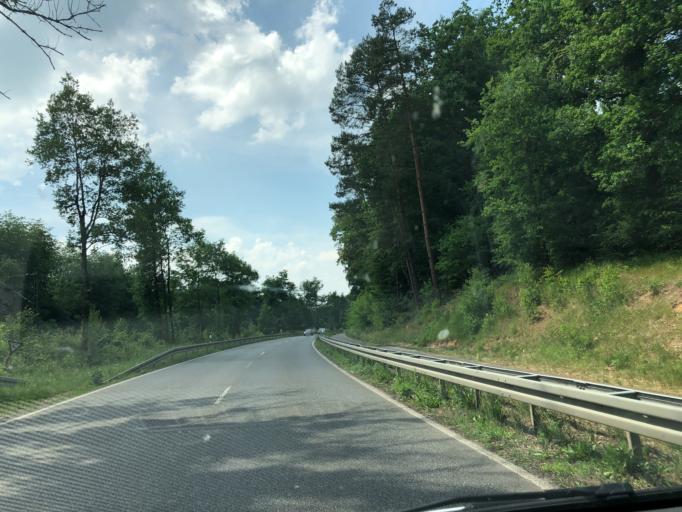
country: DE
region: Hesse
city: Neustadt (Hessen)
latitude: 50.8927
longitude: 9.1558
